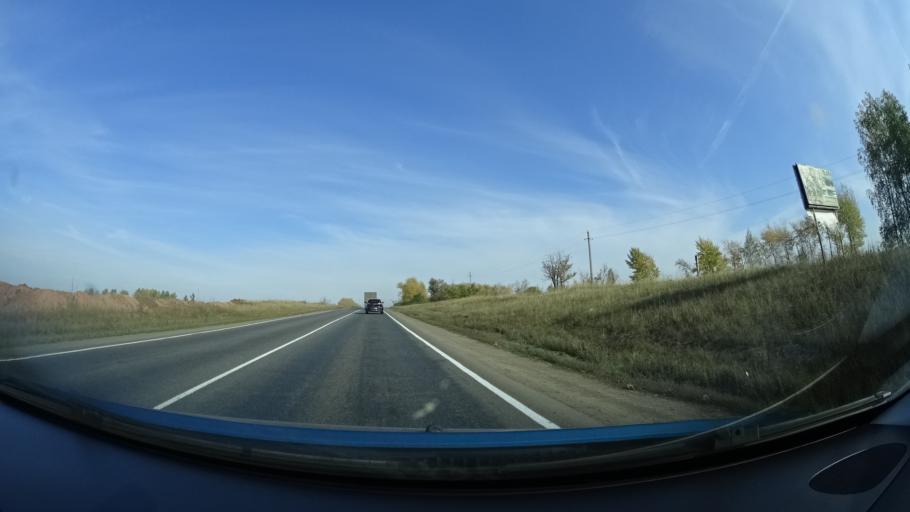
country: RU
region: Bashkortostan
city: Buzdyak
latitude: 54.6607
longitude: 54.6874
